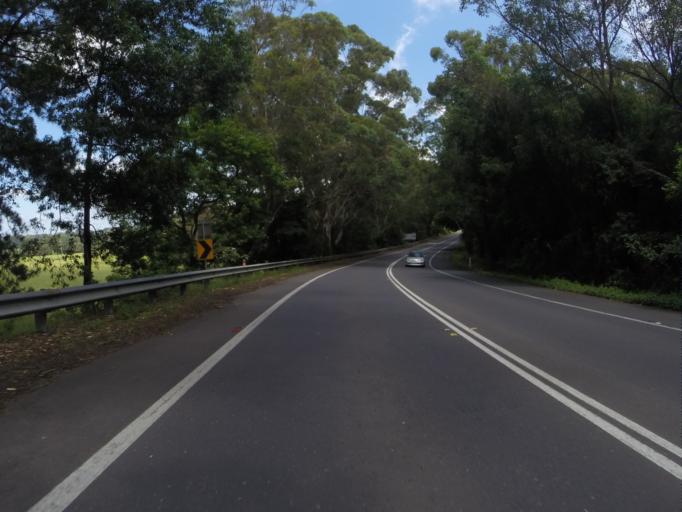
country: AU
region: New South Wales
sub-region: Shoalhaven Shire
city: Berry
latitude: -34.7631
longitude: 150.7319
